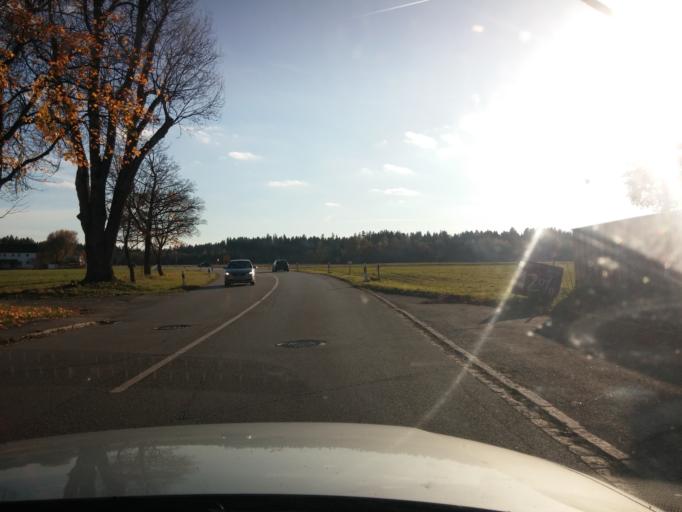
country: DE
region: Bavaria
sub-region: Upper Bavaria
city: Hohenkirchen-Siegertsbrunn
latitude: 47.9926
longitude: 11.7343
